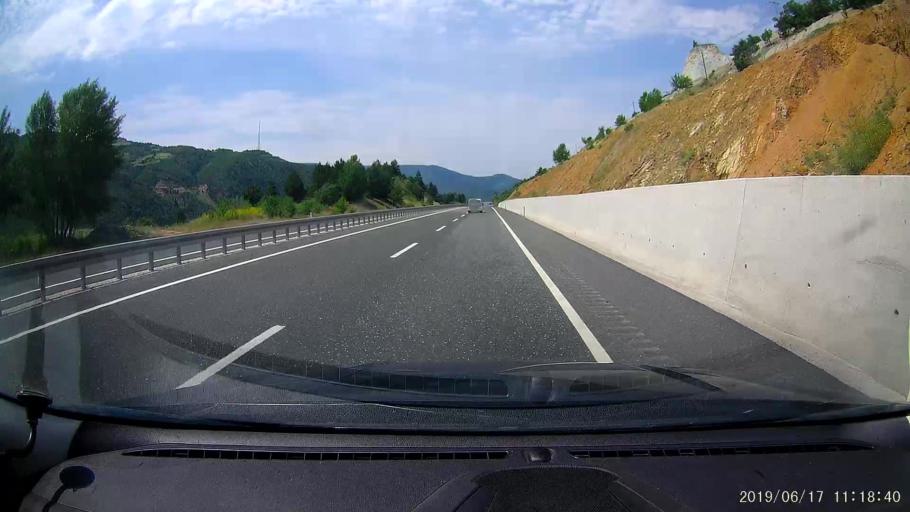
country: TR
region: Cankiri
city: Yaprakli
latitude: 40.9320
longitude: 33.8452
